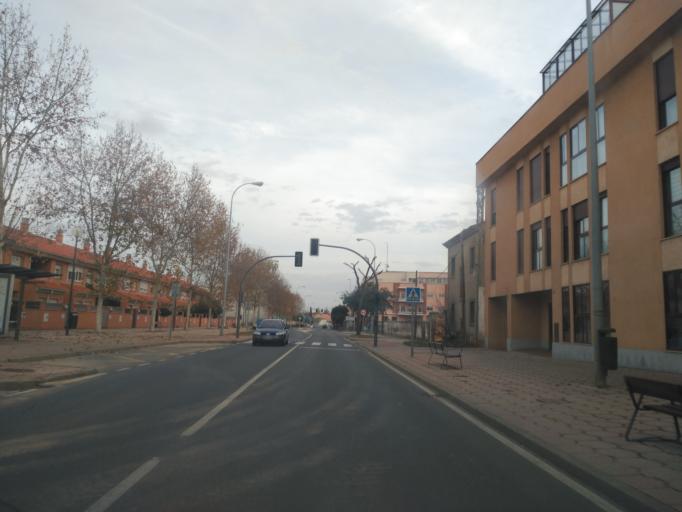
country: ES
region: Castille and Leon
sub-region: Provincia de Salamanca
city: Salamanca
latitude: 40.9550
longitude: -5.6814
